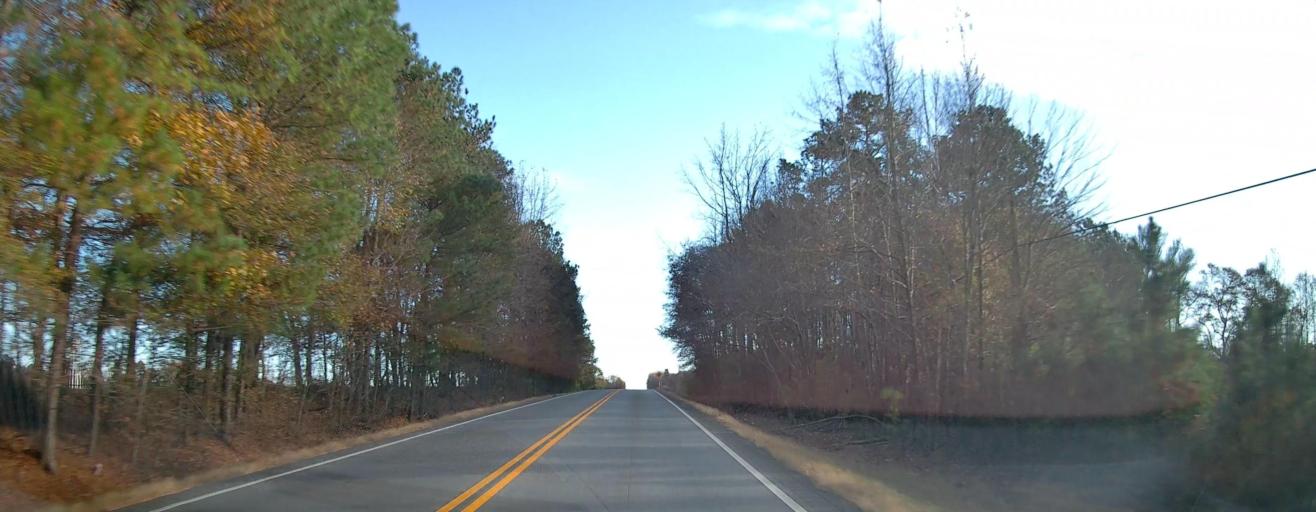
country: US
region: Alabama
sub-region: Marshall County
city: Arab
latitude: 34.2899
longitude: -86.5888
